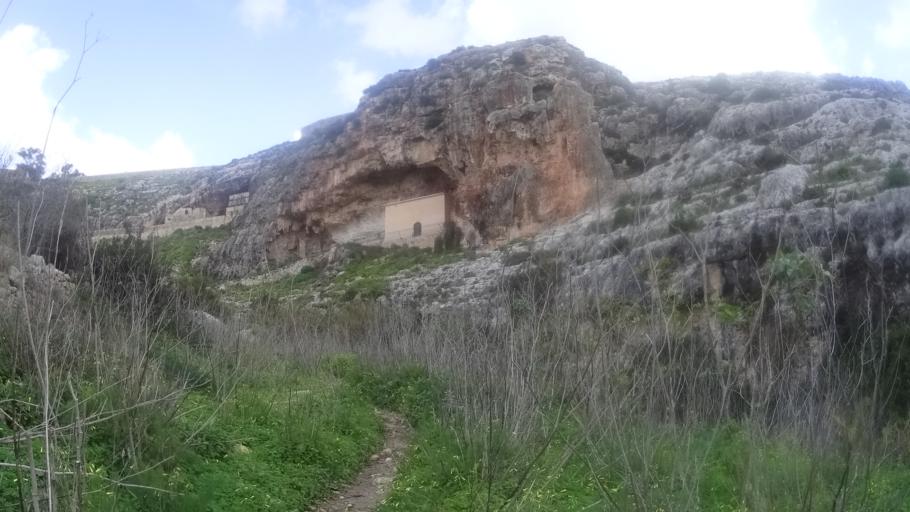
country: MT
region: Il-Mosta
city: Mosta
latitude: 35.9205
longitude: 14.4296
